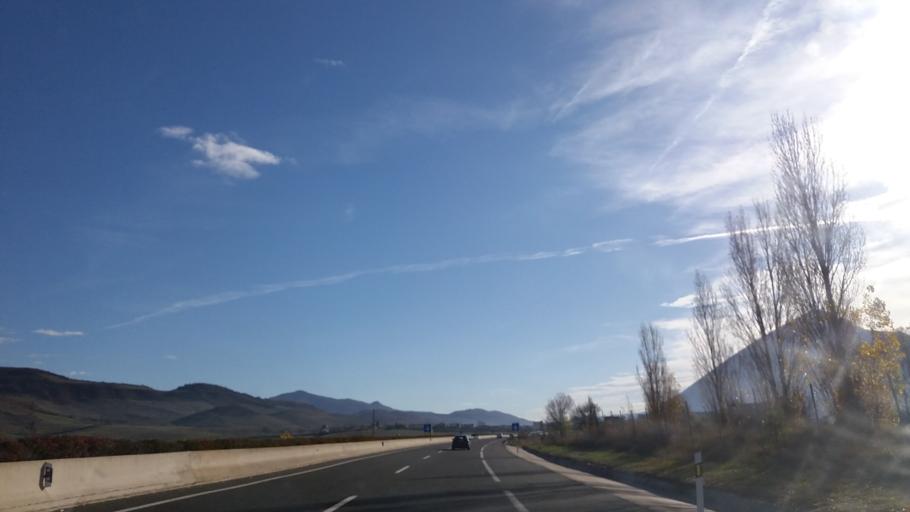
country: ES
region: Navarre
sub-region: Provincia de Navarra
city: Elorz
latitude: 42.7372
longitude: -1.5767
